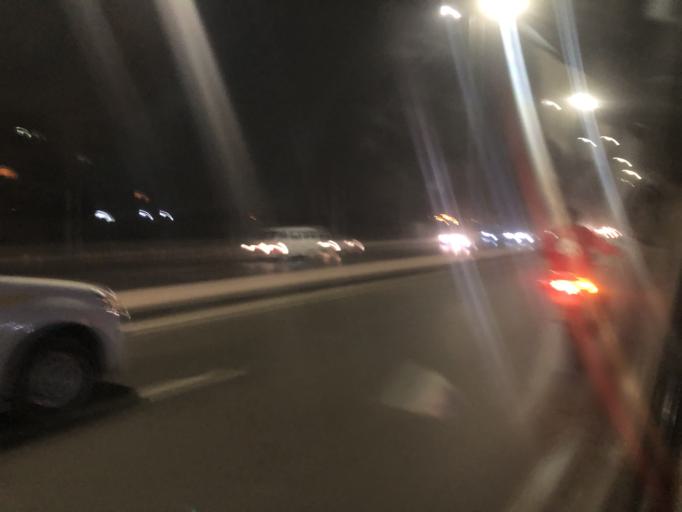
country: EG
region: Al Jizah
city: Al Jizah
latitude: 29.9833
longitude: 31.1229
